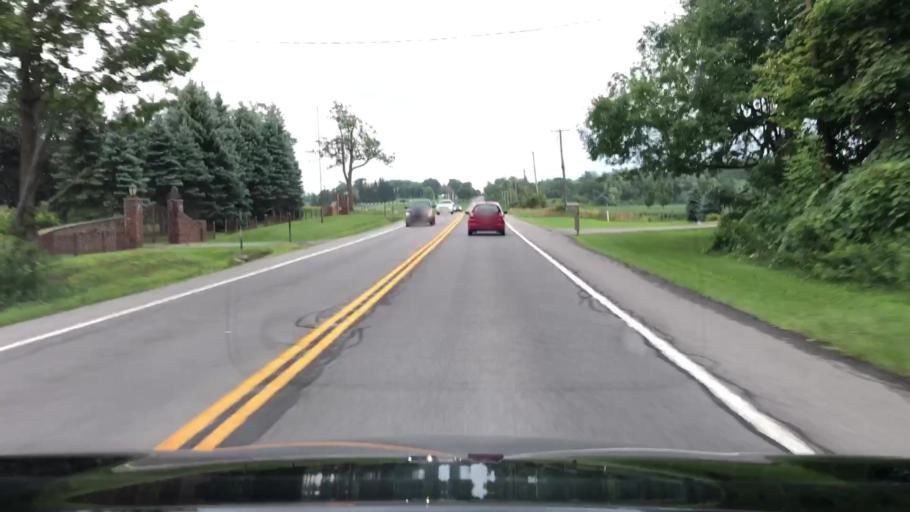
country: US
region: New York
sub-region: Erie County
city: Orchard Park
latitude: 42.7787
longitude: -78.6970
